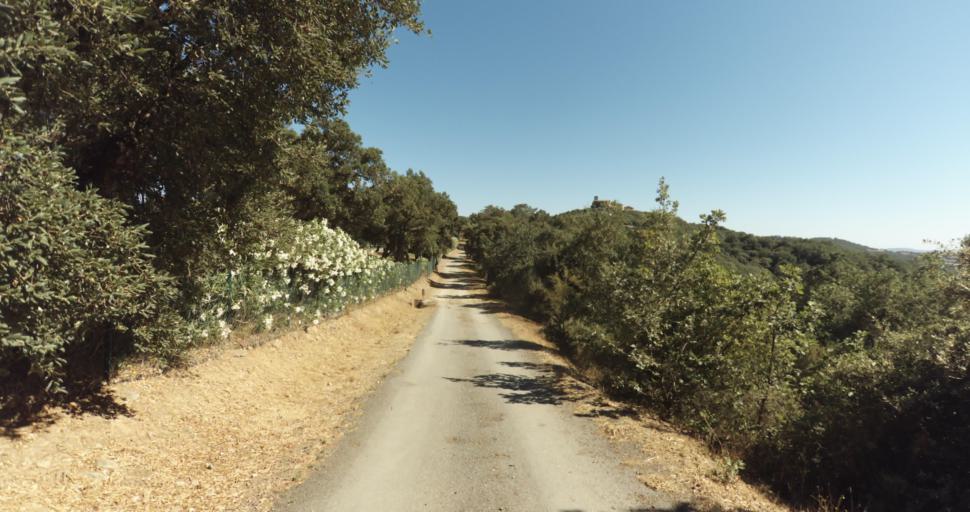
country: FR
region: Provence-Alpes-Cote d'Azur
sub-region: Departement du Var
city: Gassin
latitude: 43.2360
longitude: 6.5846
